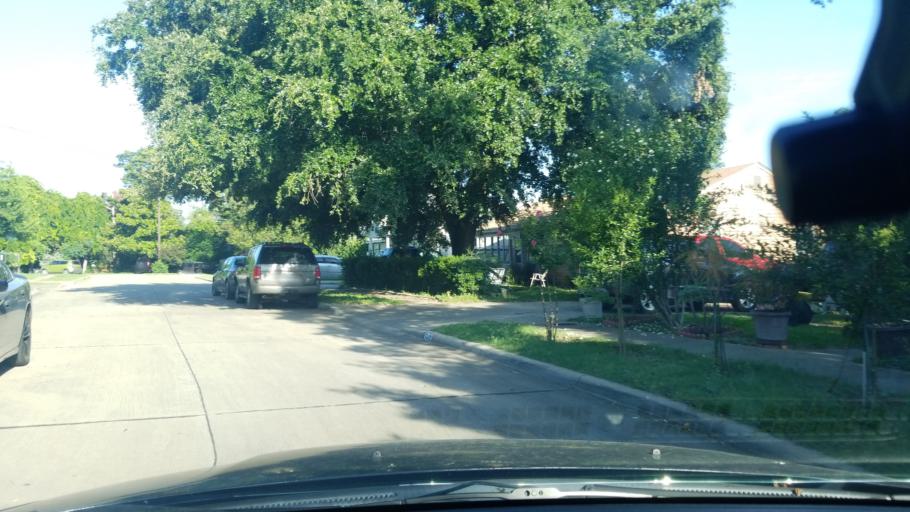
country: US
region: Texas
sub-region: Dallas County
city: Dallas
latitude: 32.7345
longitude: -96.8154
